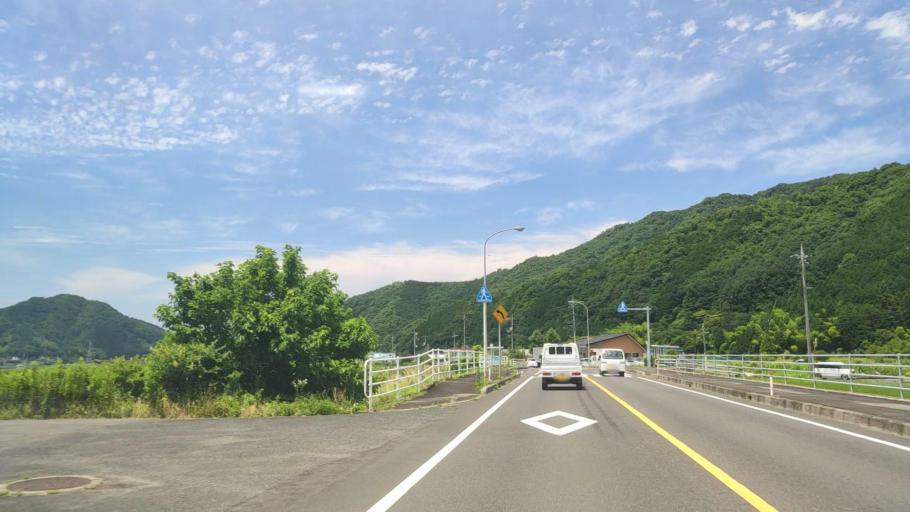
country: JP
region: Tottori
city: Tottori
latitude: 35.3716
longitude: 134.3086
